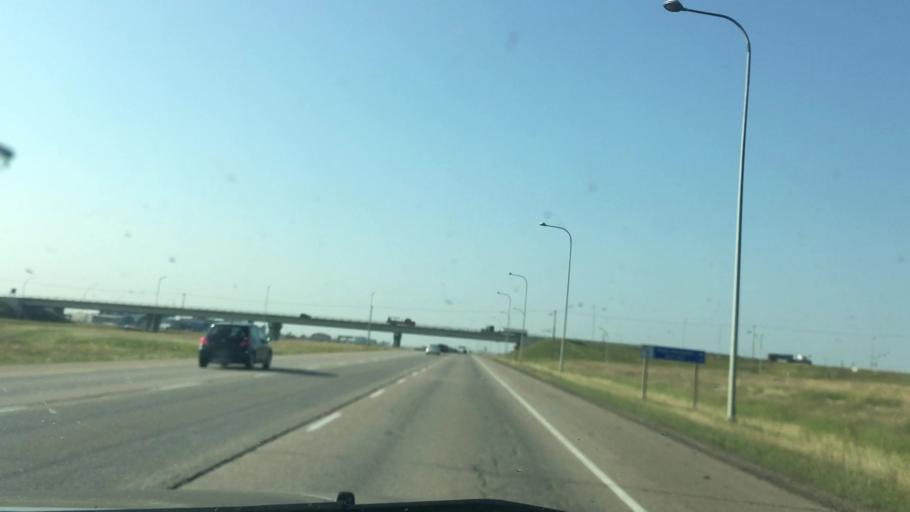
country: CA
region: Alberta
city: Leduc
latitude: 53.3118
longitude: -113.5499
